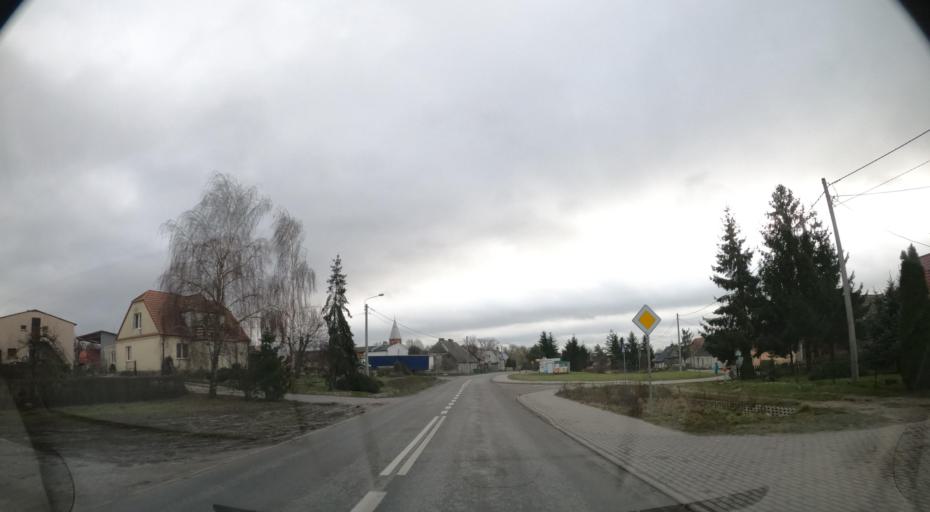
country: PL
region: Kujawsko-Pomorskie
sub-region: Powiat nakielski
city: Sadki
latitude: 53.1963
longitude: 17.3871
